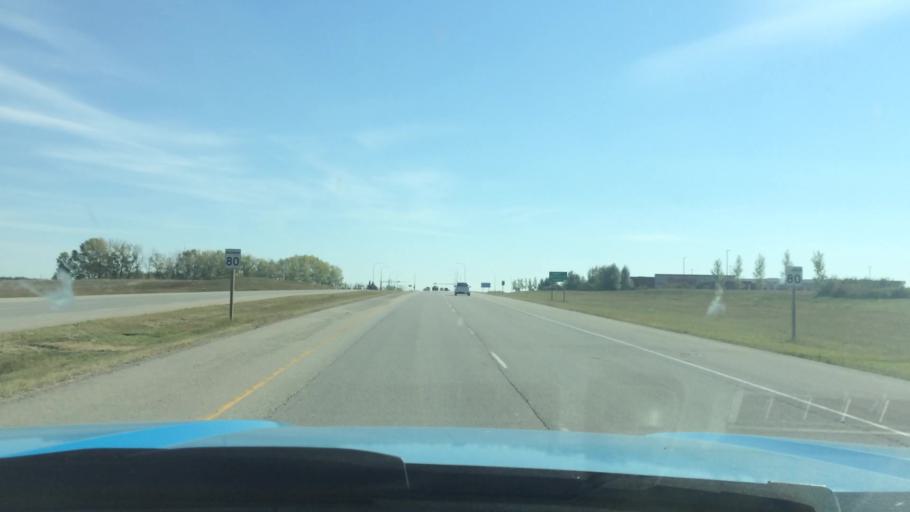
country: CA
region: Alberta
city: Airdrie
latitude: 51.2124
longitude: -113.9889
